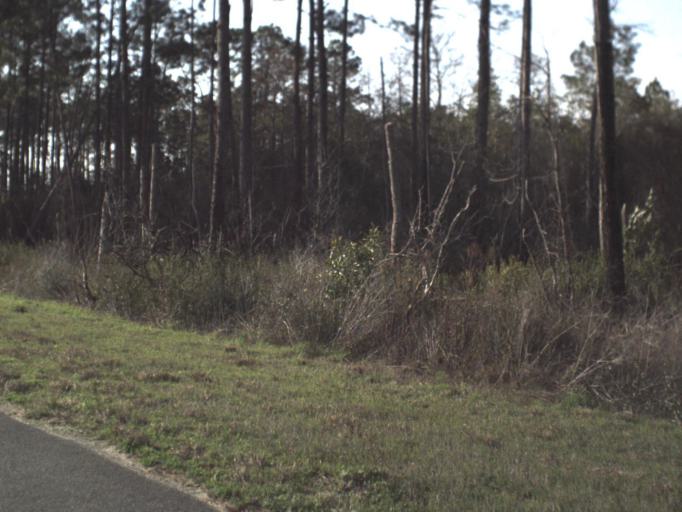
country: US
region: Florida
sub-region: Bay County
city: Laguna Beach
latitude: 30.4399
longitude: -85.8002
